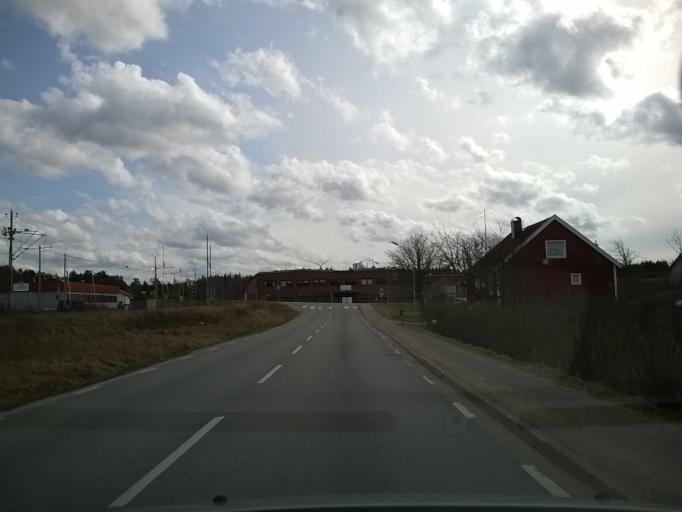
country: SE
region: Vaestra Goetaland
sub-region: Kungalvs Kommun
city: Kode
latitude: 57.9418
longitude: 11.8524
